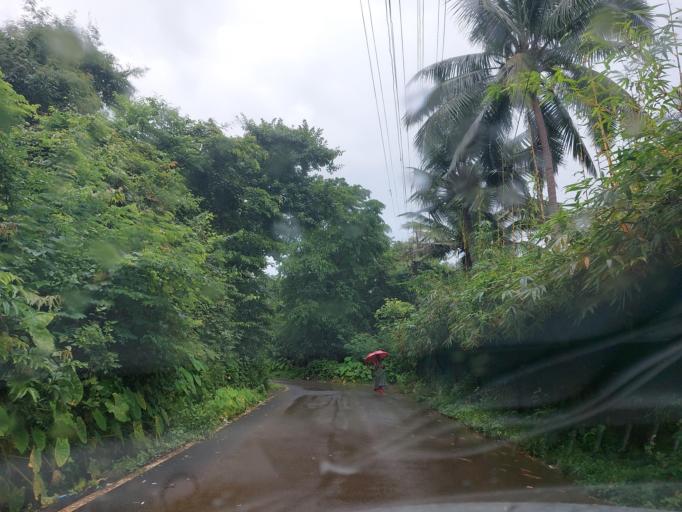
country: IN
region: Goa
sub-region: North Goa
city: Valpoy
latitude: 15.5309
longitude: 74.1309
